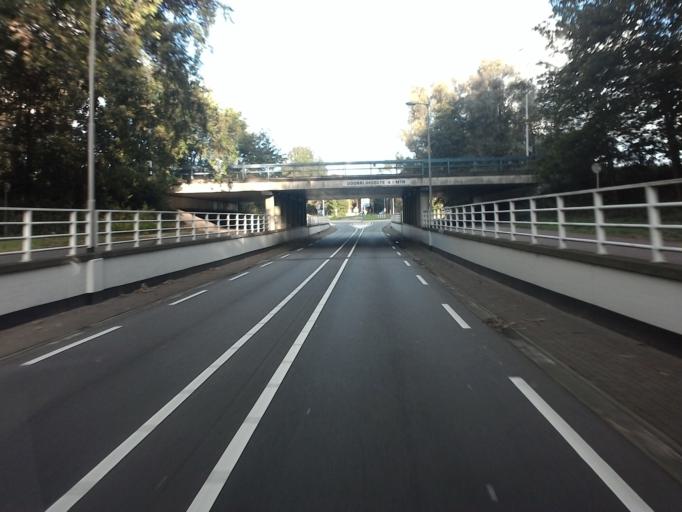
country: NL
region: North Holland
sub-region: Gemeente Beverwijk
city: Beverwijk
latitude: 52.4882
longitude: 4.6272
